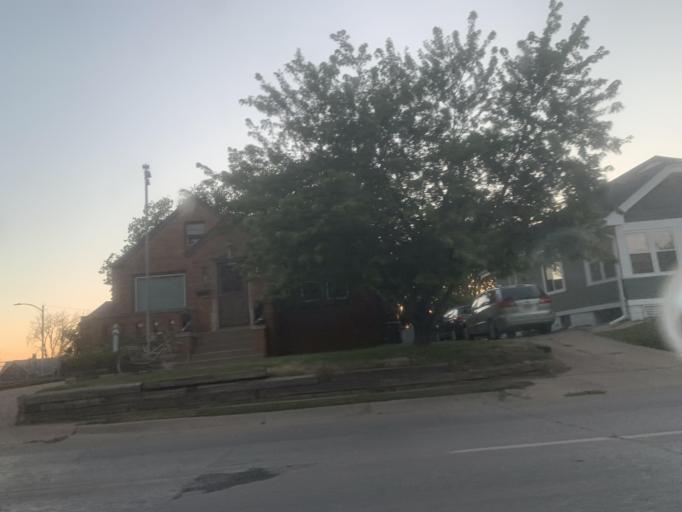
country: US
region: Nebraska
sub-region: Douglas County
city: Omaha
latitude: 41.2167
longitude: -95.9761
